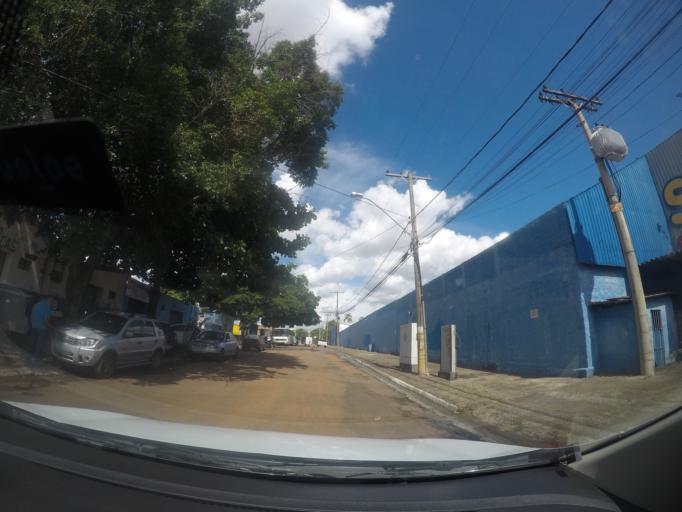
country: BR
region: Goias
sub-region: Goiania
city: Goiania
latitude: -16.6683
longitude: -49.3119
